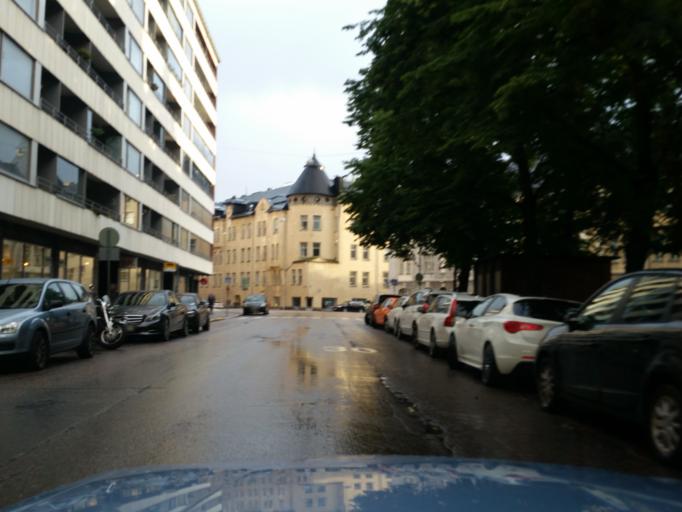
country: FI
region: Uusimaa
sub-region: Helsinki
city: Helsinki
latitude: 60.1578
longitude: 24.9456
